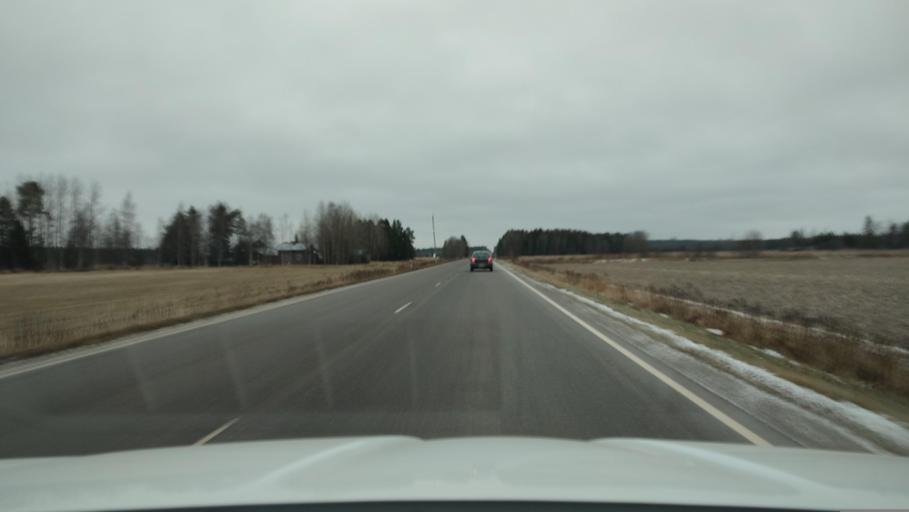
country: FI
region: Ostrobothnia
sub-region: Sydosterbotten
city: Naerpes
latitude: 62.4763
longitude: 21.4379
